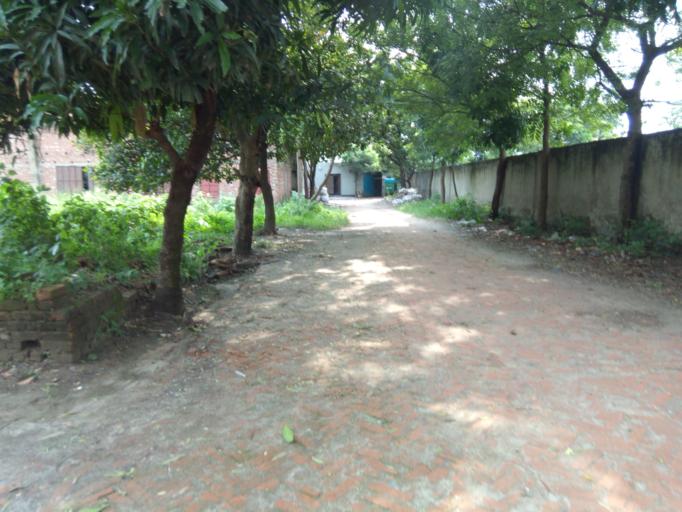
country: BD
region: Dhaka
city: Azimpur
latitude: 23.7527
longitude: 90.3422
